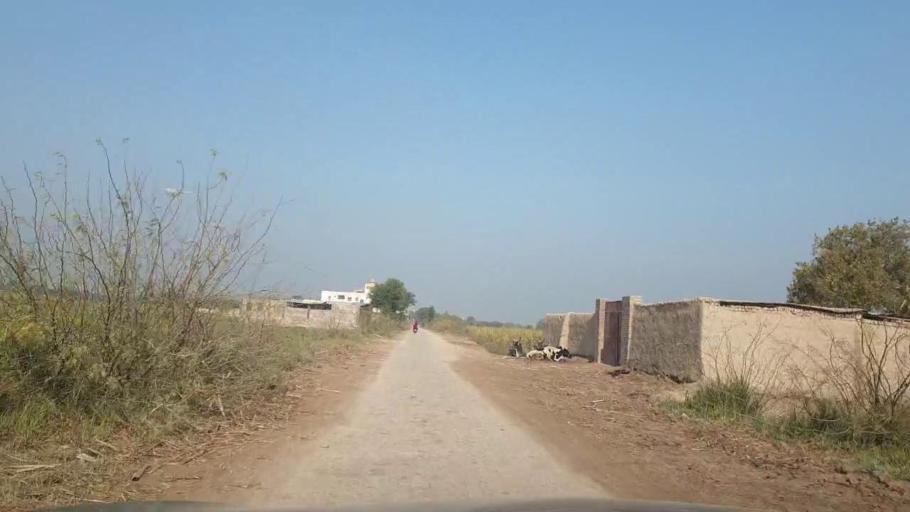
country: PK
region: Sindh
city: Tando Allahyar
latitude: 25.4988
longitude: 68.7553
